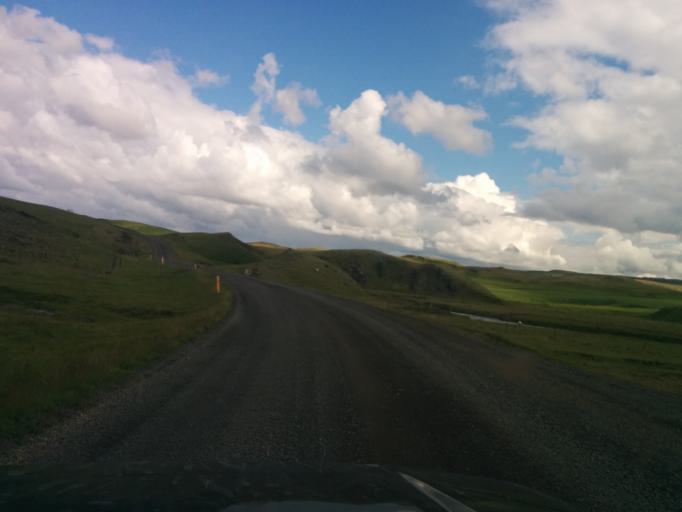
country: IS
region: South
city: Vestmannaeyjar
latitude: 63.7682
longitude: -18.4903
